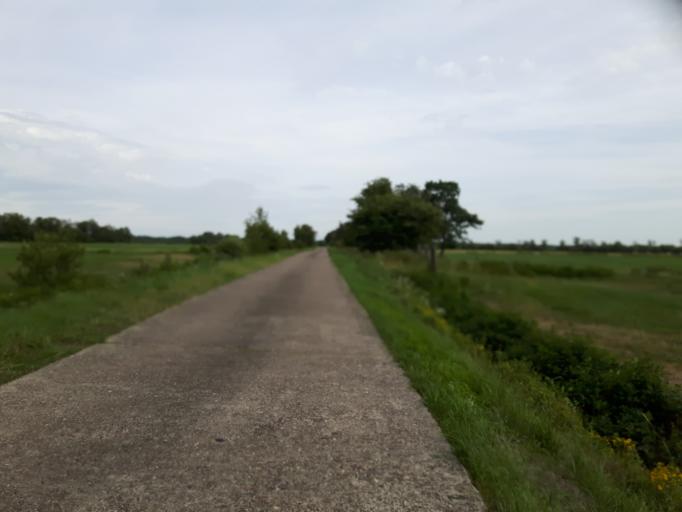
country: DE
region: Lower Saxony
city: Rastede
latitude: 53.2884
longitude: 8.2926
